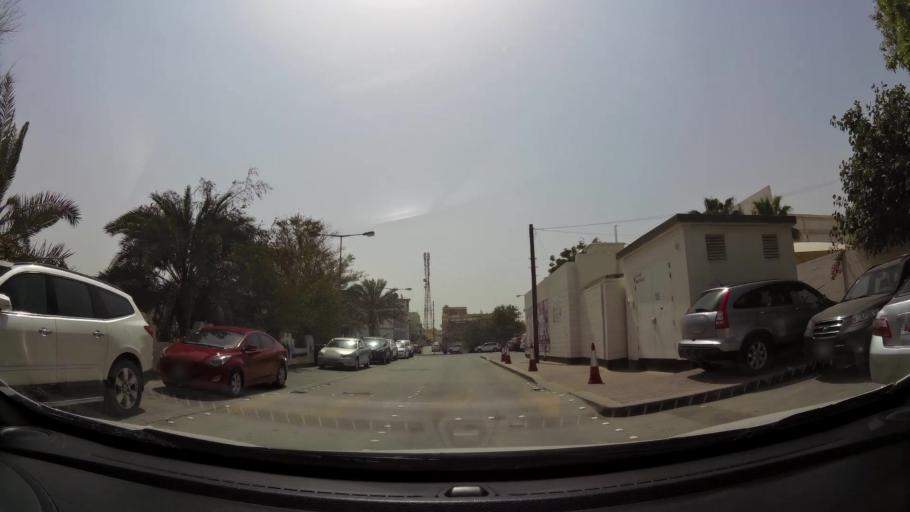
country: BH
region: Manama
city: Jidd Hafs
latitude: 26.2287
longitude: 50.4784
